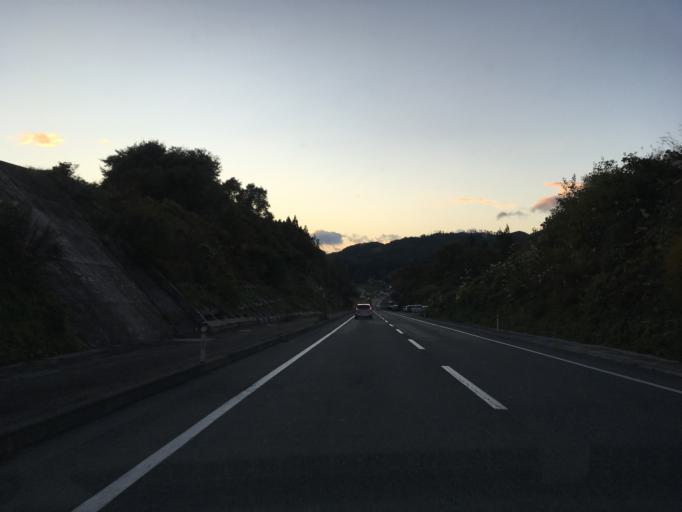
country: JP
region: Iwate
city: Kitakami
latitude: 39.2895
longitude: 141.2696
